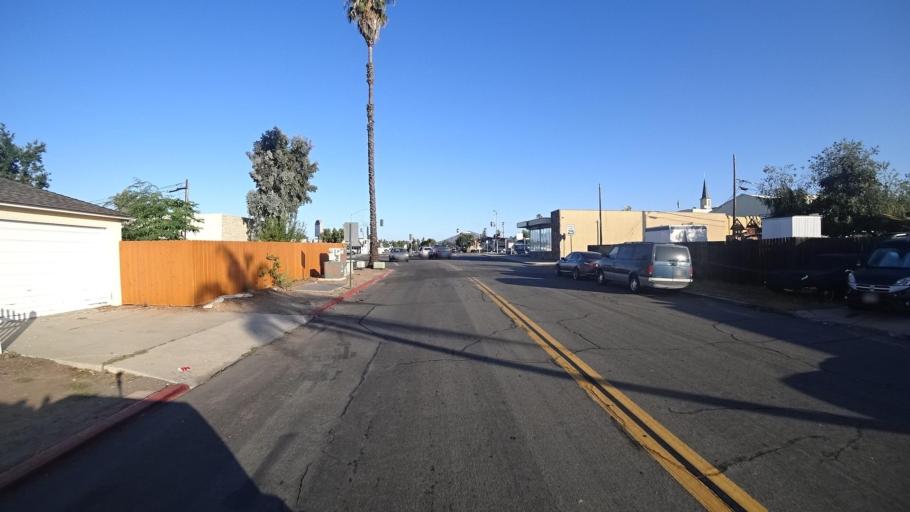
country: US
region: California
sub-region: San Diego County
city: La Mesa
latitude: 32.7701
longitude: -117.0078
